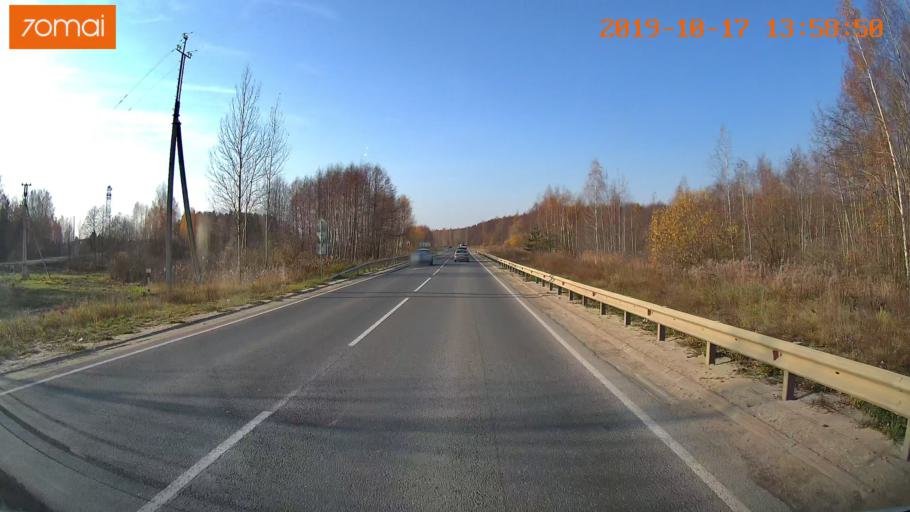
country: RU
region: Rjazan
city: Spas-Klepiki
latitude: 55.1400
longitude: 40.2163
